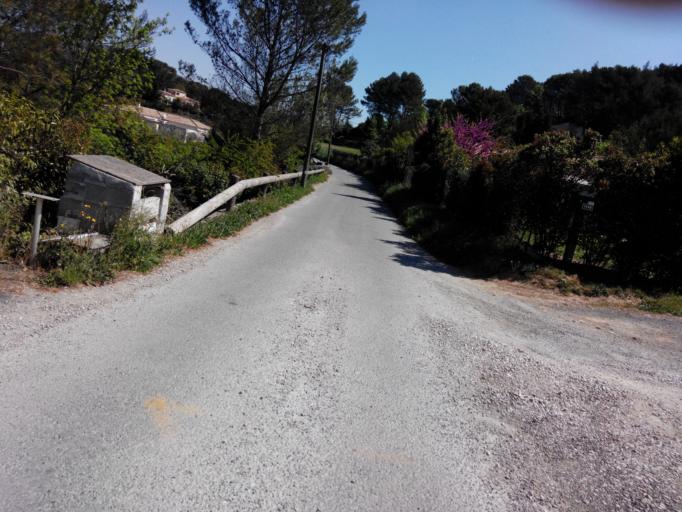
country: FR
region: Provence-Alpes-Cote d'Azur
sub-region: Departement des Bouches-du-Rhone
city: Auriol
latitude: 43.3561
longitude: 5.6320
